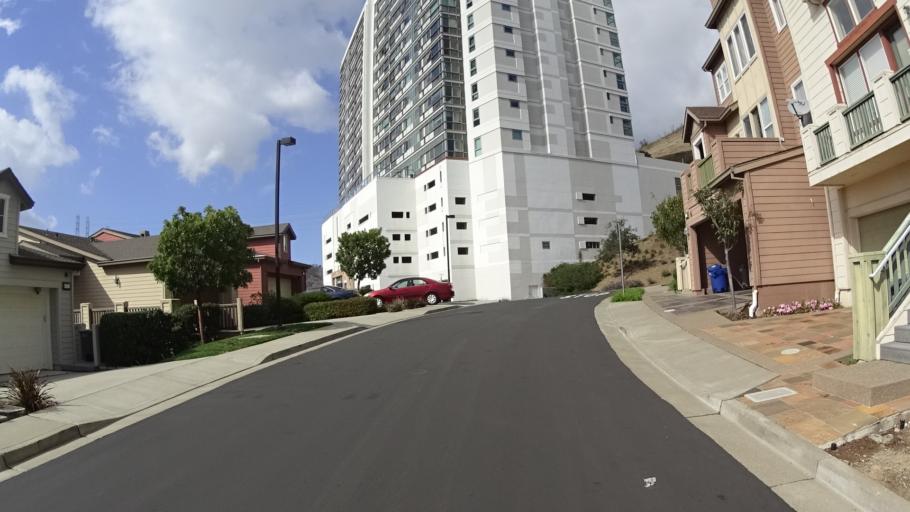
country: US
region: California
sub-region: San Mateo County
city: South San Francisco
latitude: 37.6660
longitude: -122.4029
